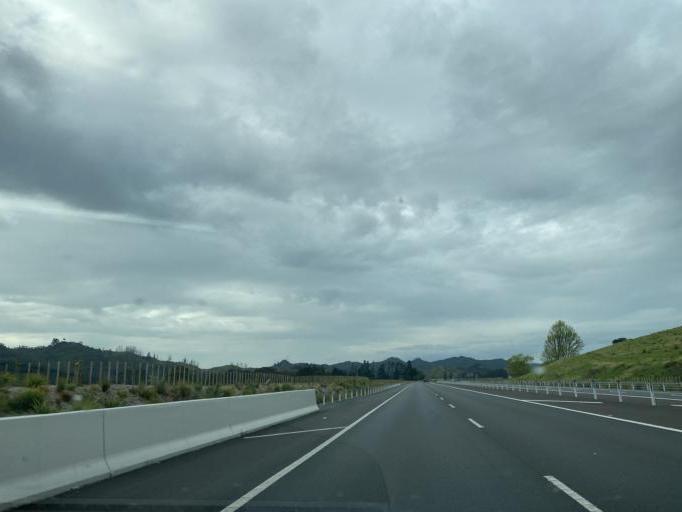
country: NZ
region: Waikato
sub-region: Waikato District
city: Ngaruawahia
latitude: -37.6121
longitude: 175.2047
